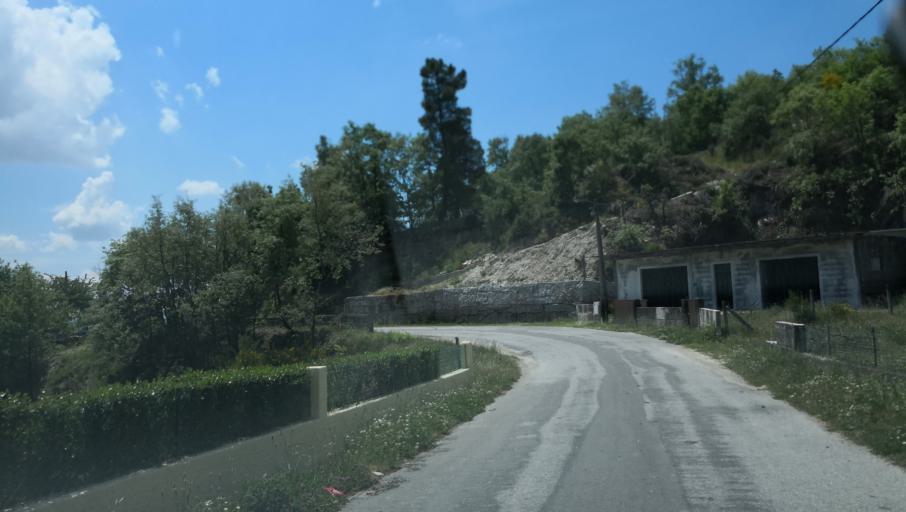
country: PT
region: Vila Real
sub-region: Vila Real
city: Vila Real
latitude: 41.3586
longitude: -7.7289
